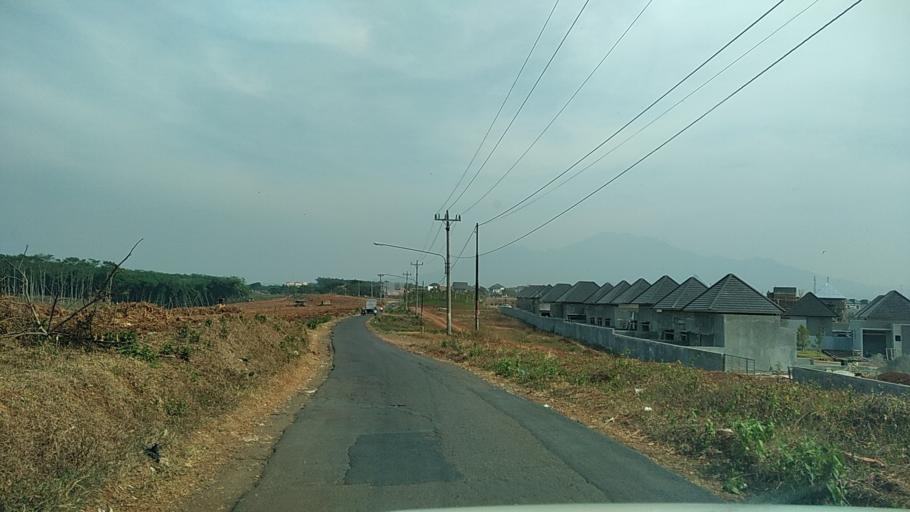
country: ID
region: Central Java
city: Semarang
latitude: -7.0370
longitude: 110.3166
